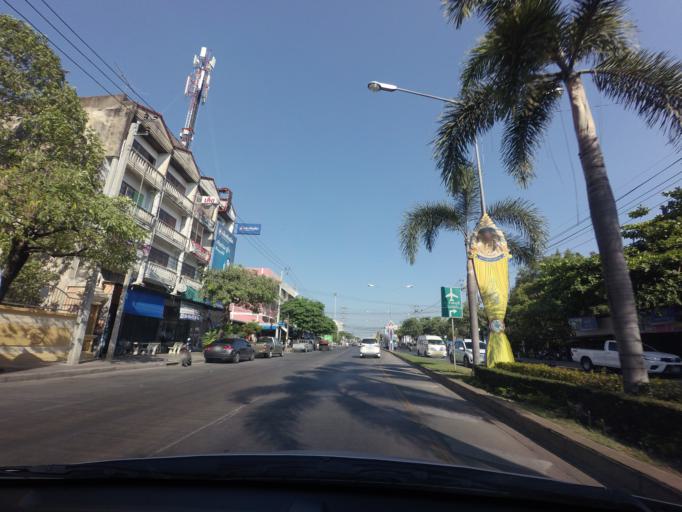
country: TH
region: Bangkok
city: Nong Chok
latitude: 13.8554
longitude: 100.8613
